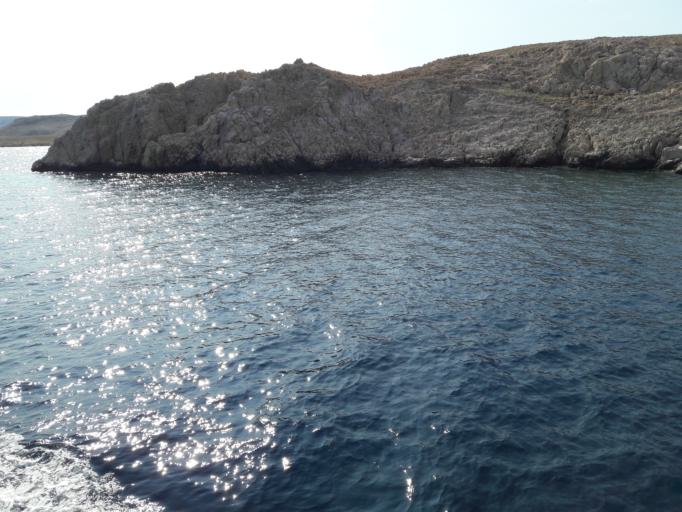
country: HR
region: Primorsko-Goranska
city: Banjol
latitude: 44.7042
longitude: 14.8696
